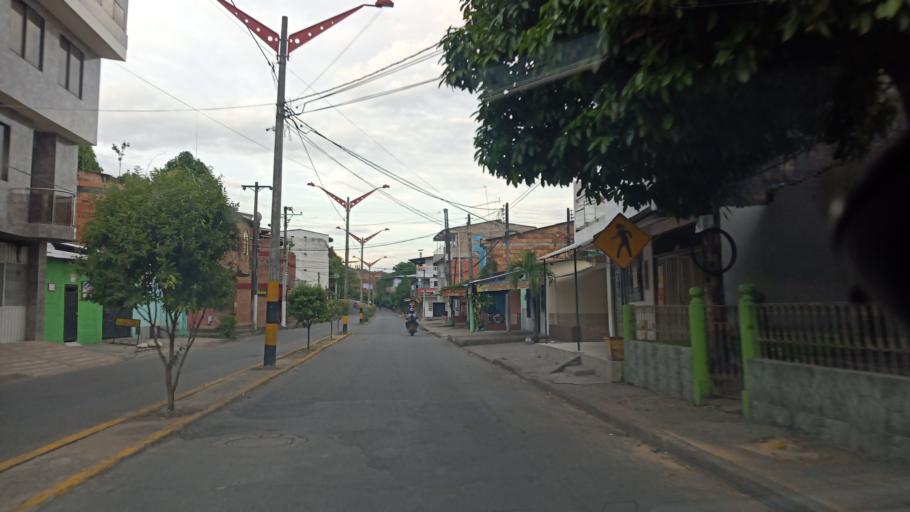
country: CO
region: Tolima
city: Melgar
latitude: 4.2022
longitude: -74.6470
